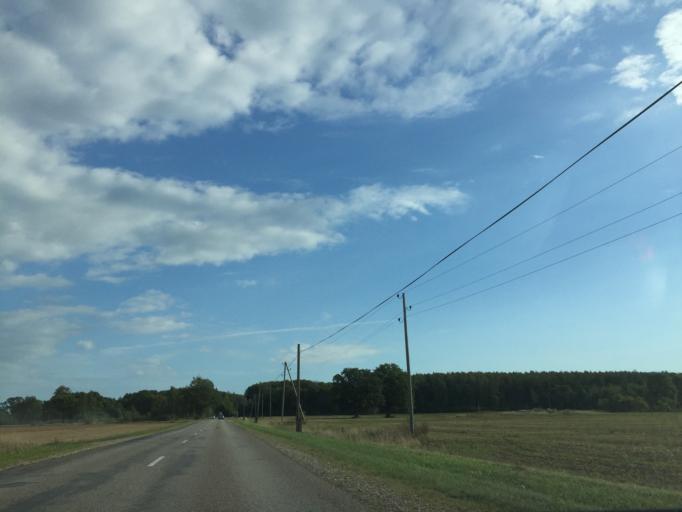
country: LV
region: Limbazu Rajons
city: Limbazi
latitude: 57.5125
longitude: 24.5172
